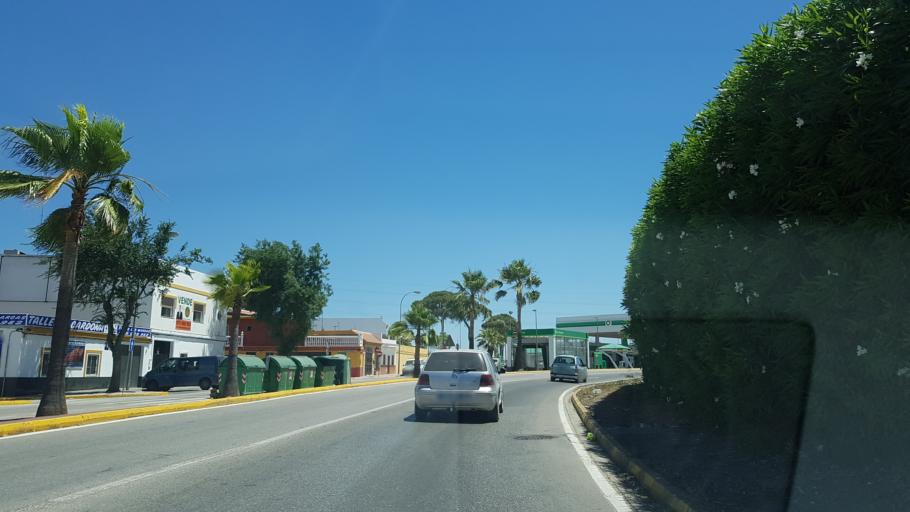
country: ES
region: Andalusia
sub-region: Provincia de Sevilla
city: Dos Hermanas
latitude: 37.2905
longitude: -5.9005
